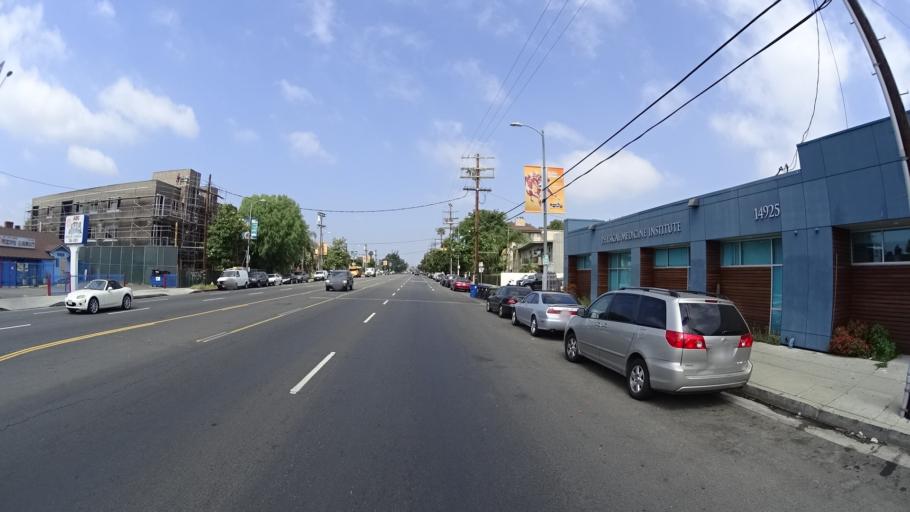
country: US
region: California
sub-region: Los Angeles County
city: Van Nuys
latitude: 34.1722
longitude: -118.4582
